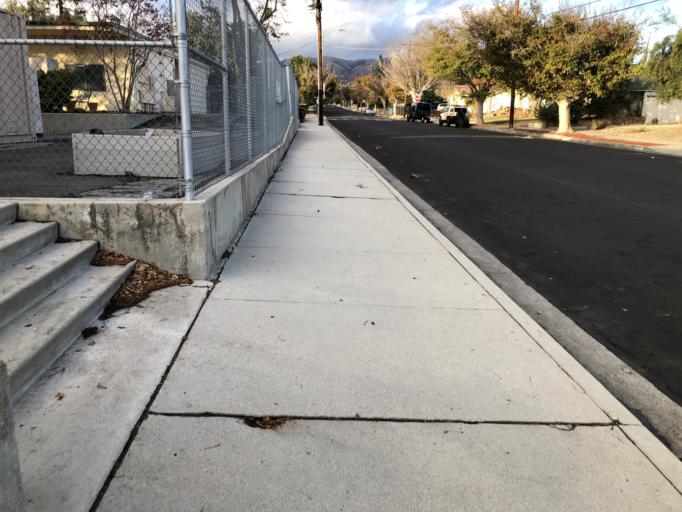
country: US
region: California
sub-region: Los Angeles County
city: Chatsworth
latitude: 34.2619
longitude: -118.5843
